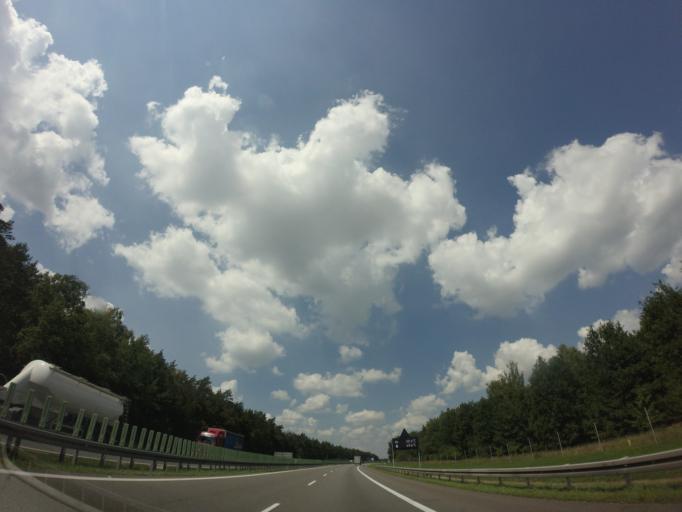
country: PL
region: Opole Voivodeship
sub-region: Powiat krapkowicki
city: Krapkowice
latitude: 50.4917
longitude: 17.9801
